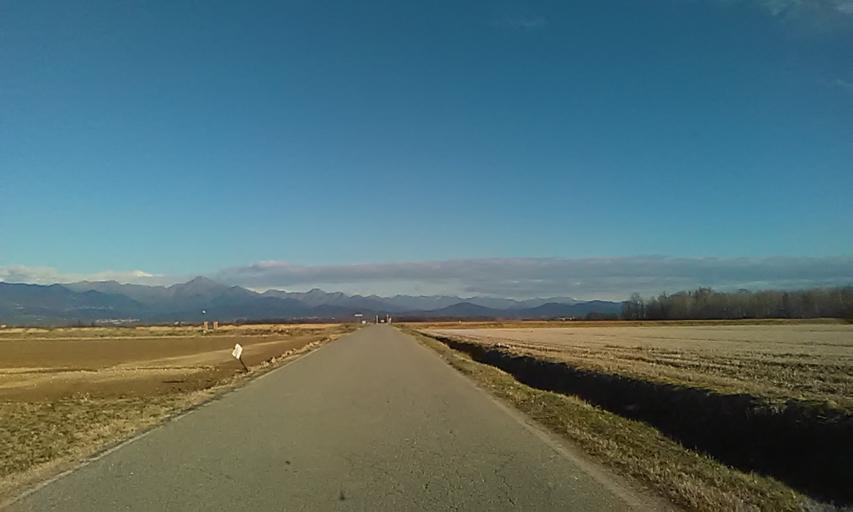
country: IT
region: Piedmont
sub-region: Provincia di Vercelli
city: Rovasenda
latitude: 45.5256
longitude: 8.2765
